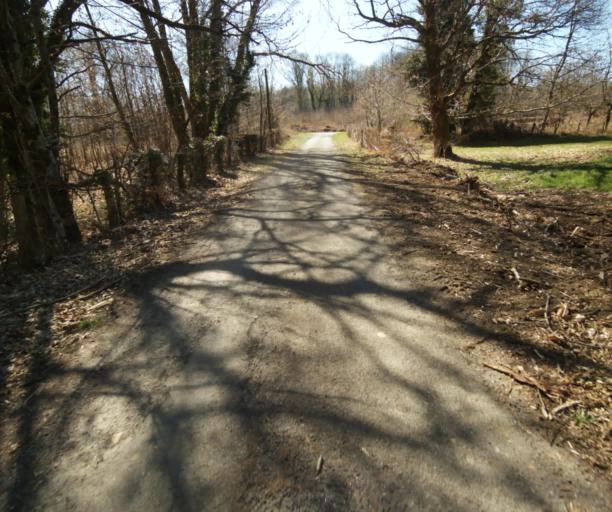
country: FR
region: Limousin
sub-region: Departement de la Correze
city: Saint-Clement
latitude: 45.3901
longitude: 1.6518
